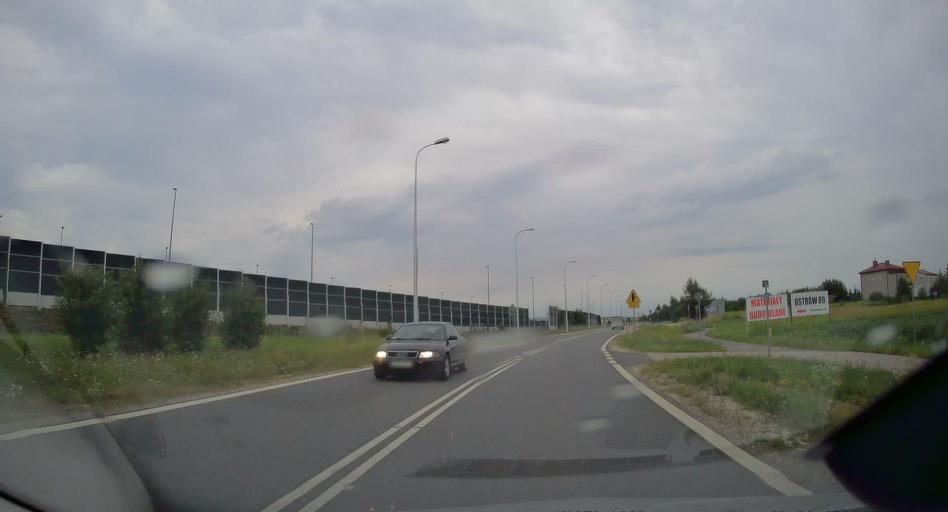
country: PL
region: Lesser Poland Voivodeship
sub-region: Powiat tarnowski
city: Wierzchoslawice
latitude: 50.0134
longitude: 20.8702
